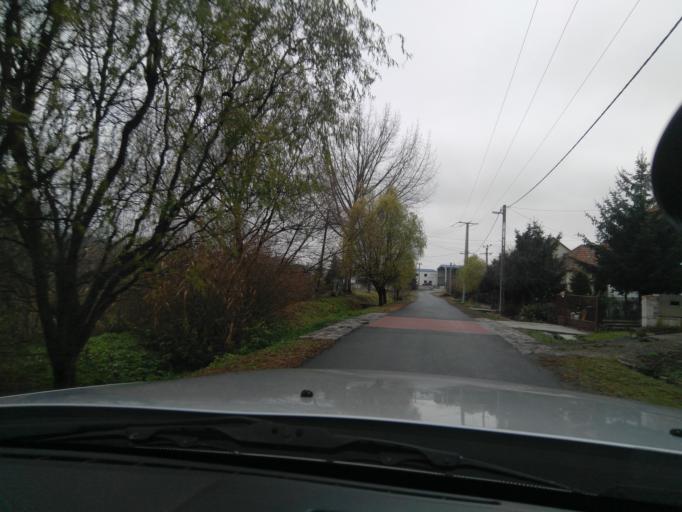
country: HU
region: Nograd
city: Matraterenye
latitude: 48.0290
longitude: 19.9537
